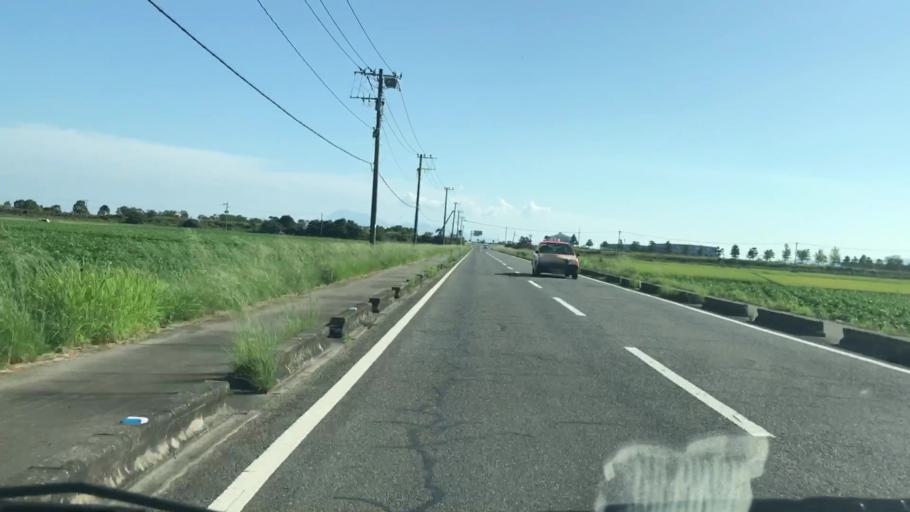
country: JP
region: Saga Prefecture
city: Okawa
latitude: 33.1569
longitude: 130.3082
